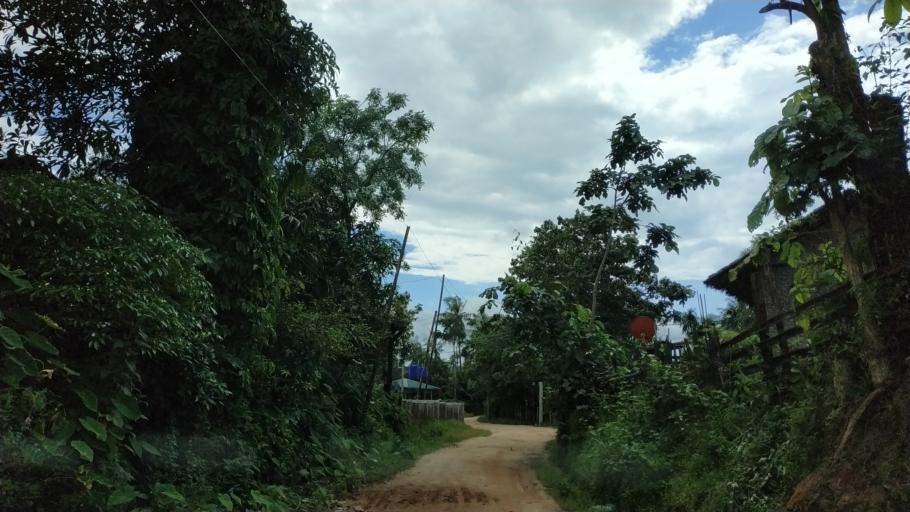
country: MM
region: Tanintharyi
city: Dawei
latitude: 14.1868
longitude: 98.1643
